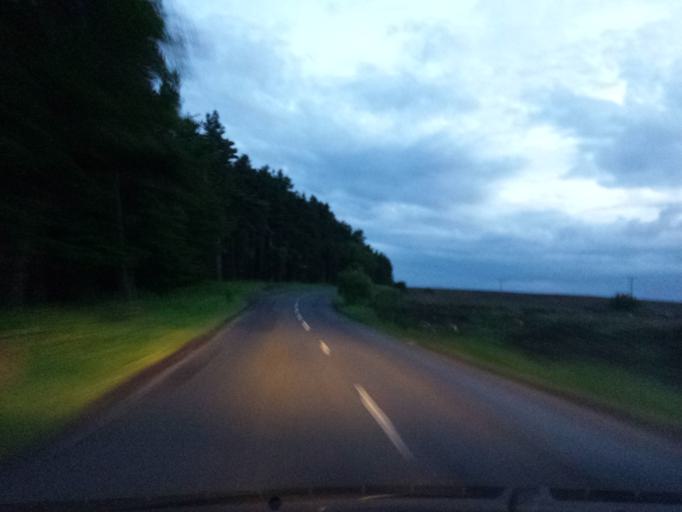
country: GB
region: Scotland
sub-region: The Scottish Borders
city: Duns
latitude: 55.7287
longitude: -2.4452
